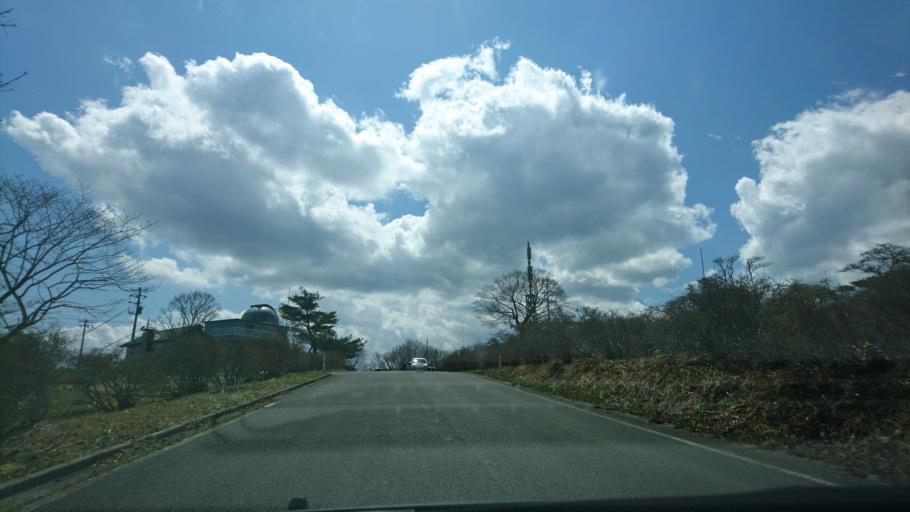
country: JP
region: Iwate
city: Ofunato
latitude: 38.9731
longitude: 141.4458
